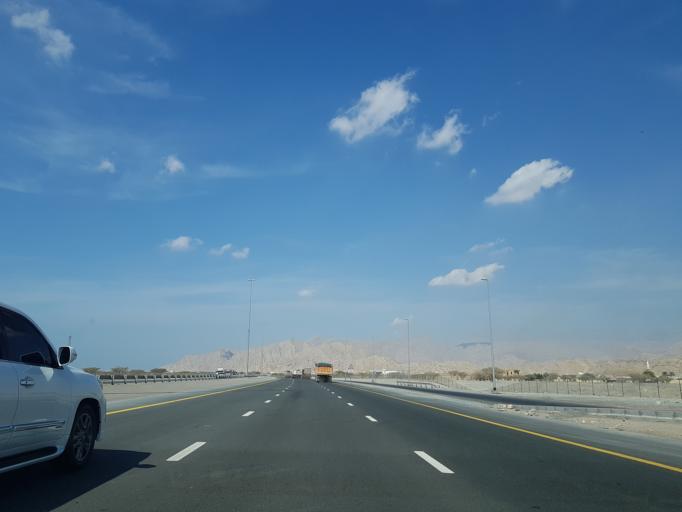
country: AE
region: Ra's al Khaymah
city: Ras al-Khaimah
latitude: 25.7812
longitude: 56.0312
